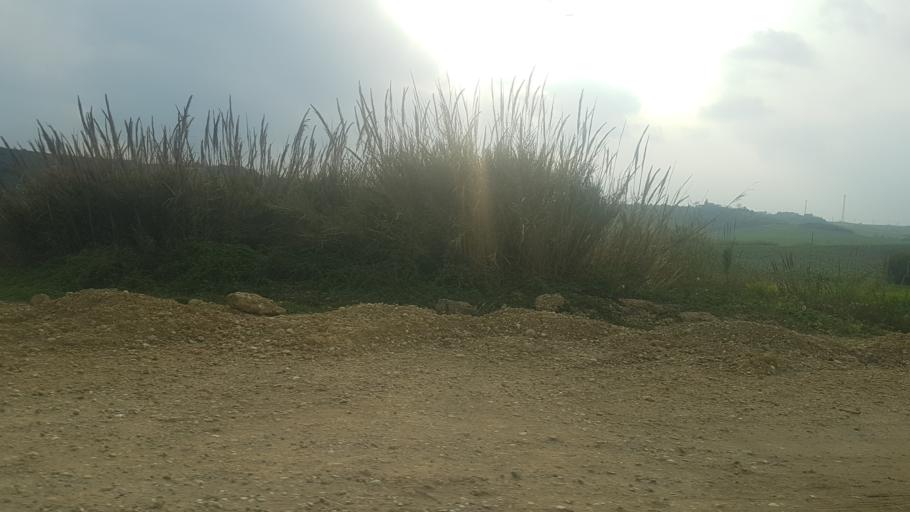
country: TR
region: Adana
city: Seyhan
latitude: 37.0444
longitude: 35.2123
